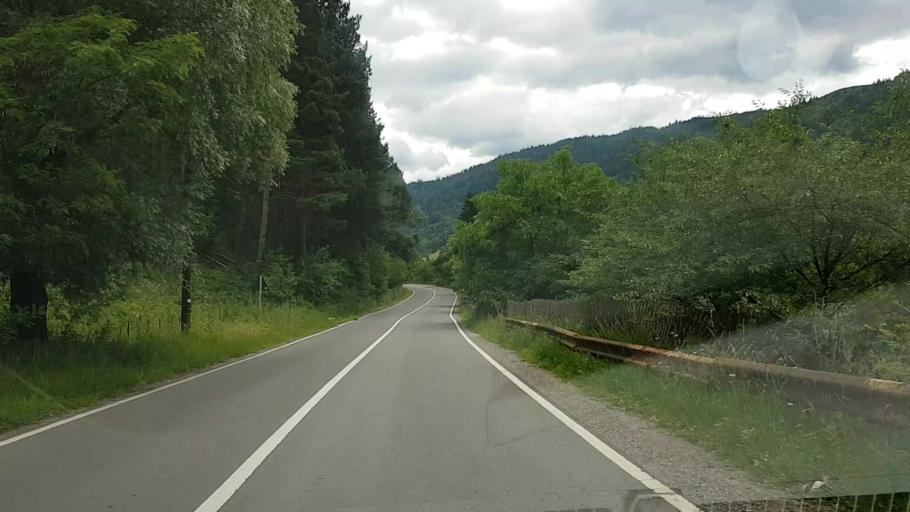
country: RO
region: Neamt
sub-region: Comuna Farcasa
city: Farcasa
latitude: 47.1335
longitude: 25.8982
